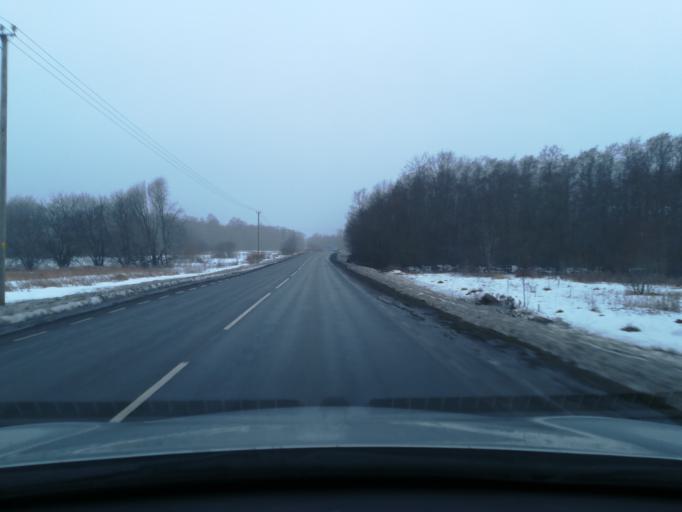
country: EE
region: Harju
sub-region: Rae vald
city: Jueri
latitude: 59.3676
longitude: 24.9210
